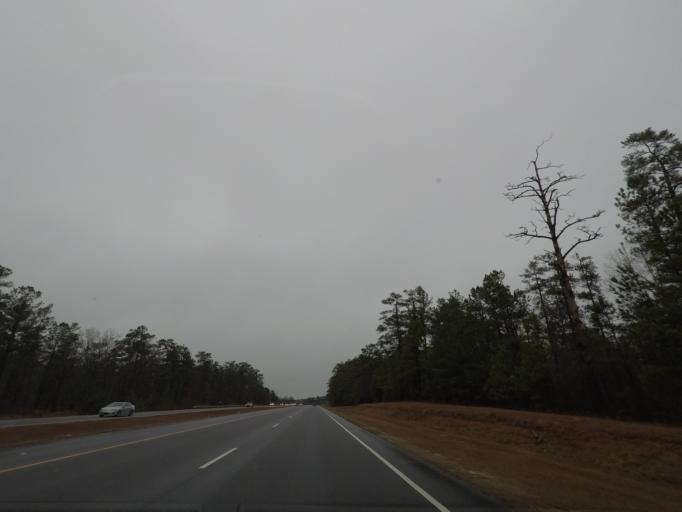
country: US
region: North Carolina
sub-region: Cumberland County
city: Spring Lake
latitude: 35.2398
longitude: -79.0211
